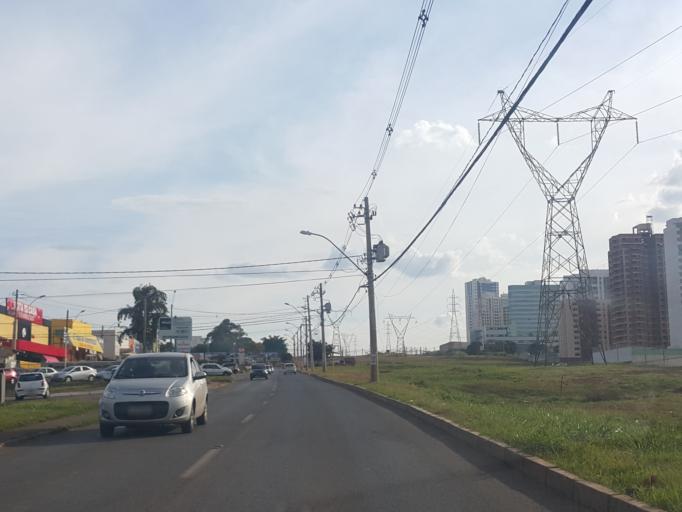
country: BR
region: Federal District
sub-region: Brasilia
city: Brasilia
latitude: -15.8455
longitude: -48.0233
